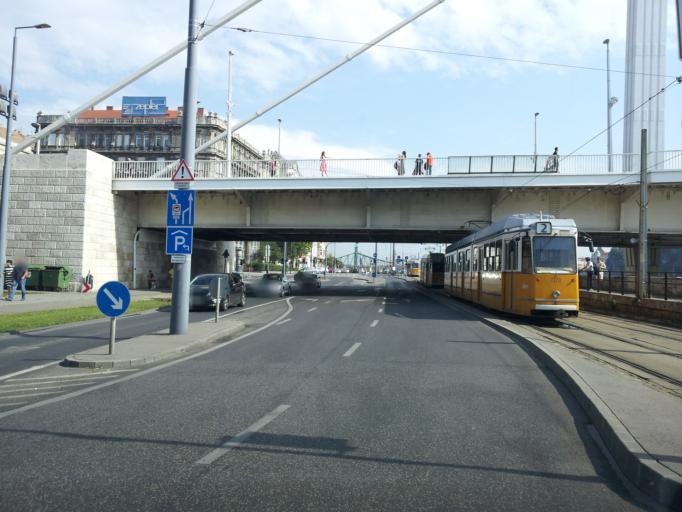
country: HU
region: Budapest
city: Budapest I. keruelet
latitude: 47.4920
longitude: 19.0508
